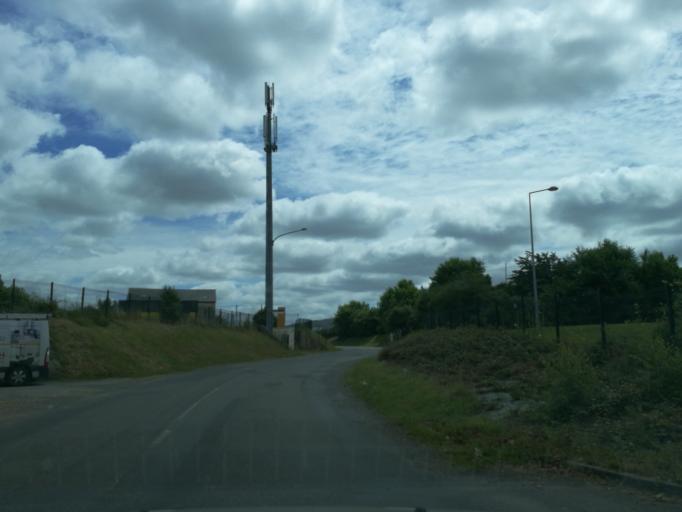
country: FR
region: Brittany
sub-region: Departement d'Ille-et-Vilaine
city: Bedee
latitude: 48.1831
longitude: -1.9415
